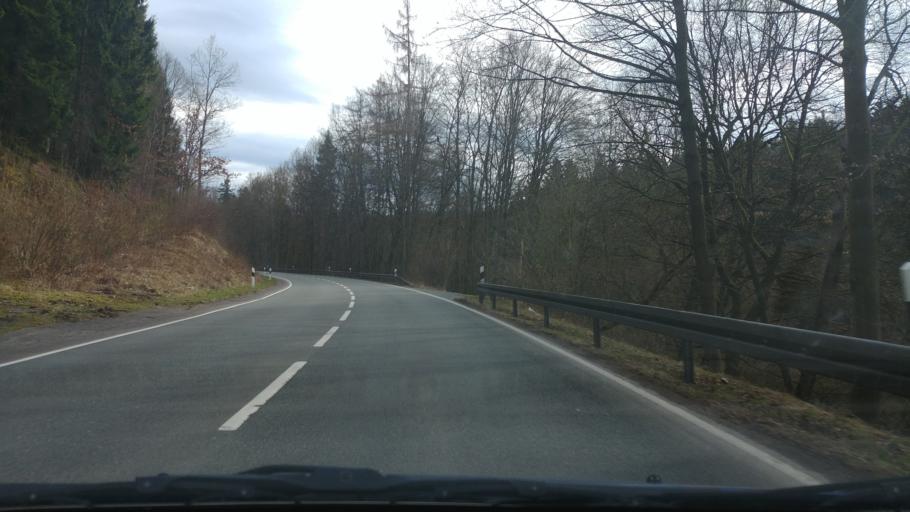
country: DE
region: Lower Saxony
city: Bevern
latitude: 51.8094
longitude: 9.4949
